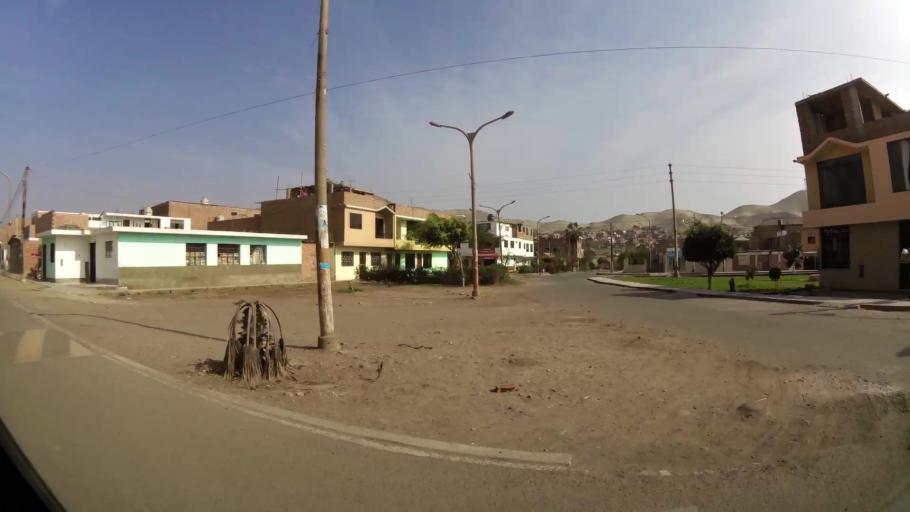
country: PE
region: Lima
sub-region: Lima
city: Santa Rosa
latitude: -11.7741
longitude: -77.1696
